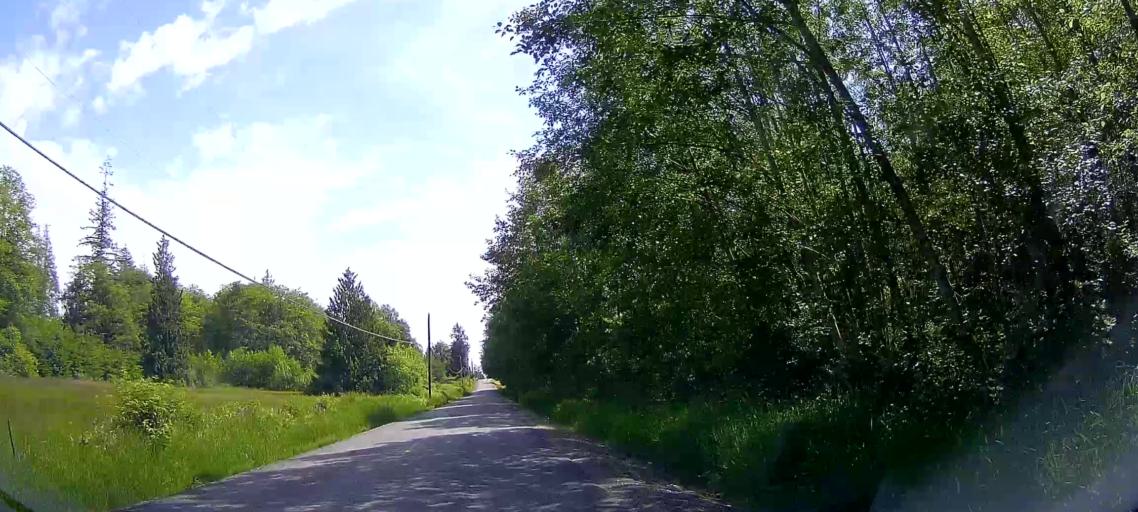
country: US
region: Washington
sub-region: Skagit County
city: Burlington
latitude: 48.5657
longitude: -122.3618
